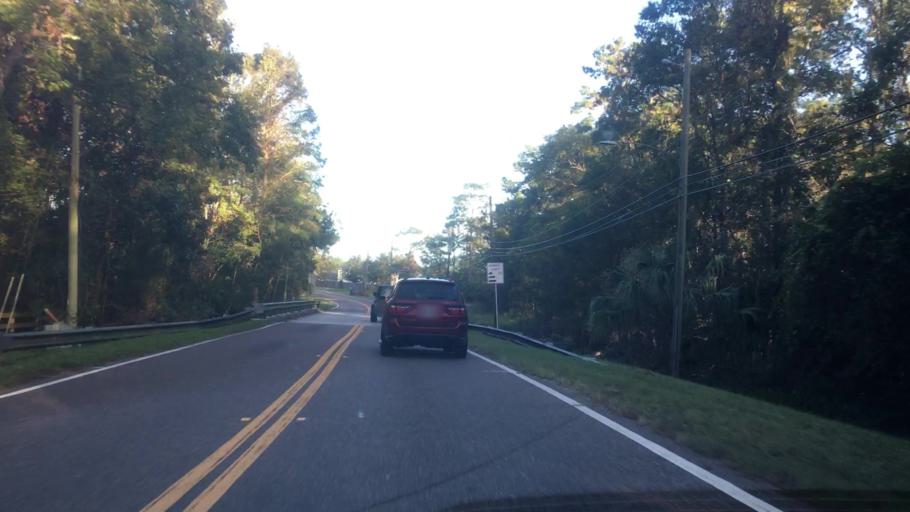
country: US
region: Florida
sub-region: Duval County
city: Jacksonville
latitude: 30.4706
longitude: -81.6013
